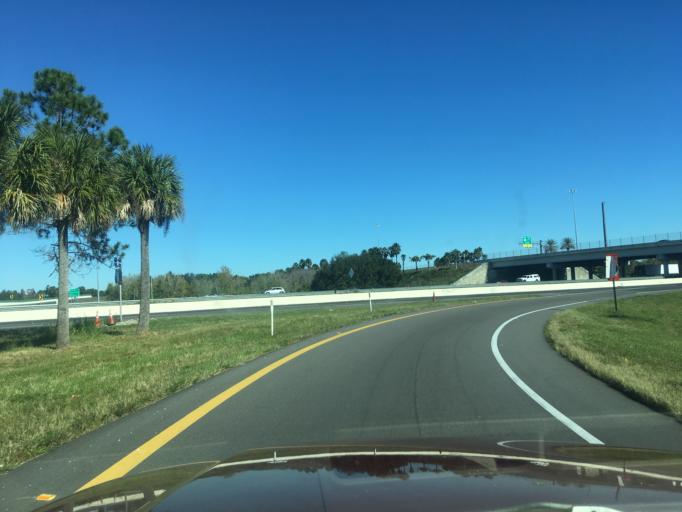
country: US
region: Florida
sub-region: Hillsborough County
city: East Lake-Orient Park
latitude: 27.9953
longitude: -82.3594
